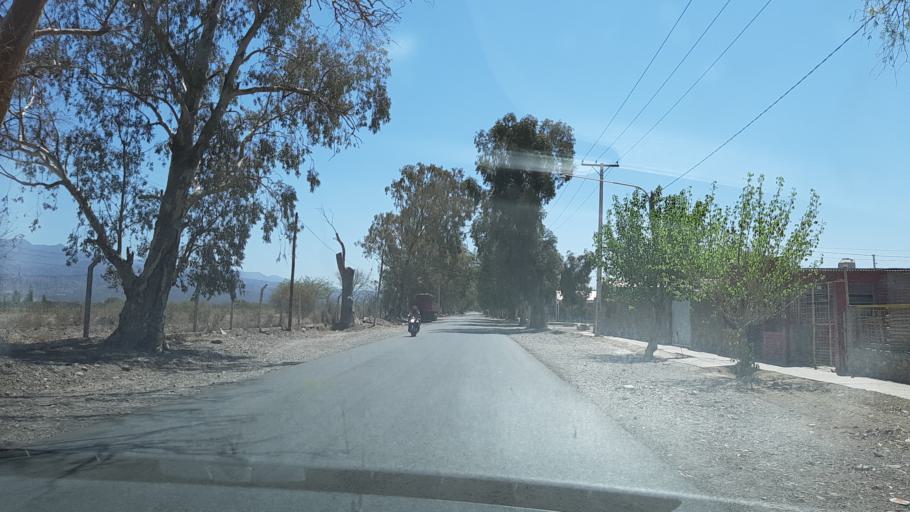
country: AR
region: San Juan
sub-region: Departamento de Zonda
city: Zonda
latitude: -31.5395
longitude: -68.7524
